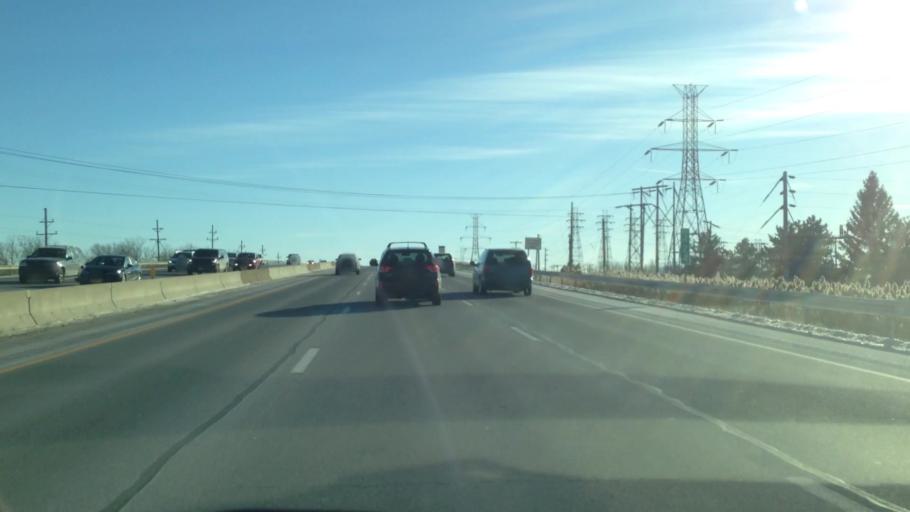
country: US
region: New York
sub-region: Erie County
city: Cheektowaga
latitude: 42.8977
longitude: -78.7673
